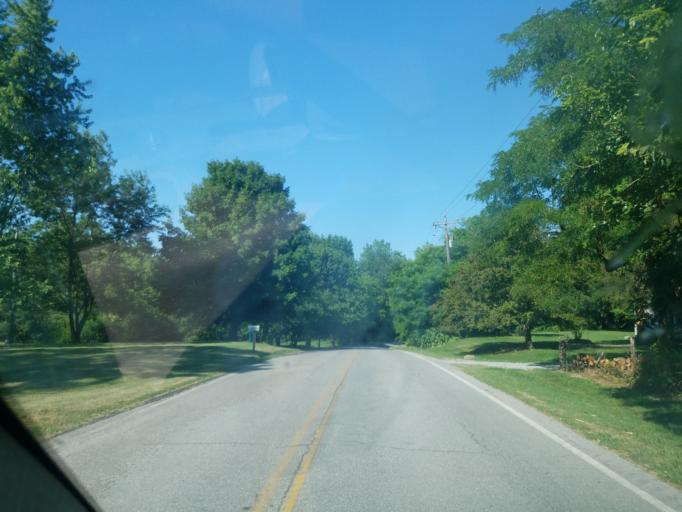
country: US
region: Ohio
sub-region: Union County
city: Richwood
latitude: 40.4150
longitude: -83.4506
